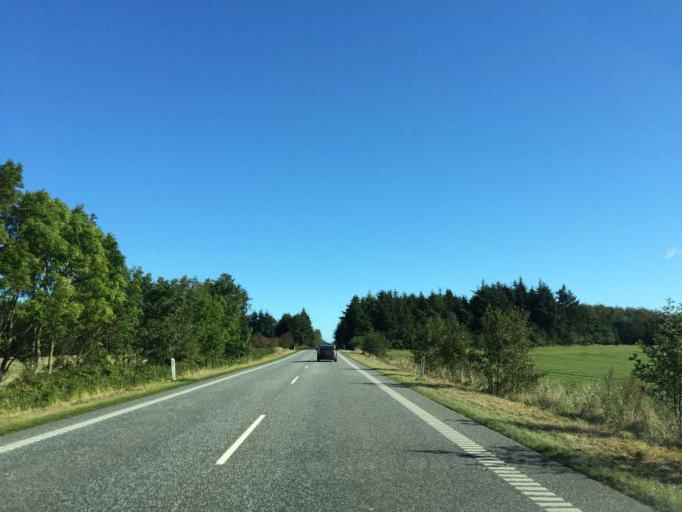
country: DK
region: Central Jutland
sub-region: Viborg Kommune
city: Stoholm
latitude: 56.4119
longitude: 9.0207
